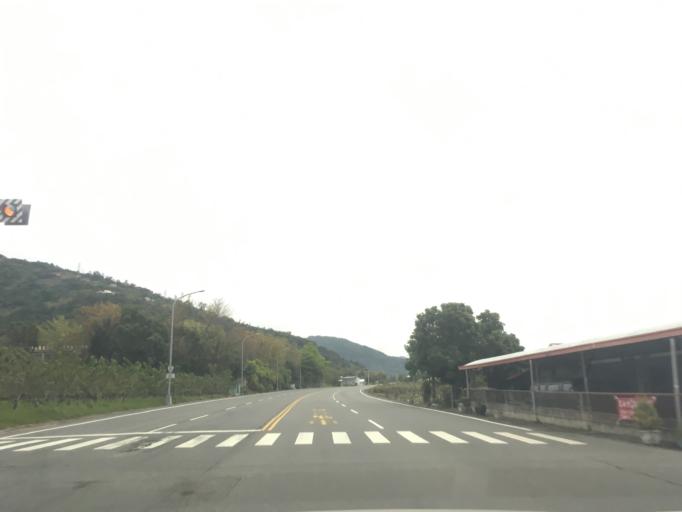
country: TW
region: Taiwan
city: Taitung City
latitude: 22.7300
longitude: 121.0561
